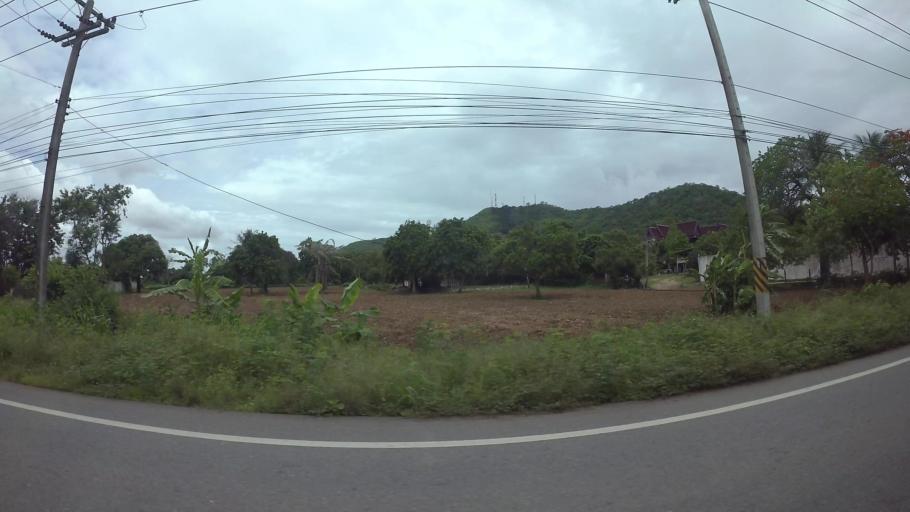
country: TH
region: Chon Buri
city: Si Racha
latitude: 13.1959
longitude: 100.9610
